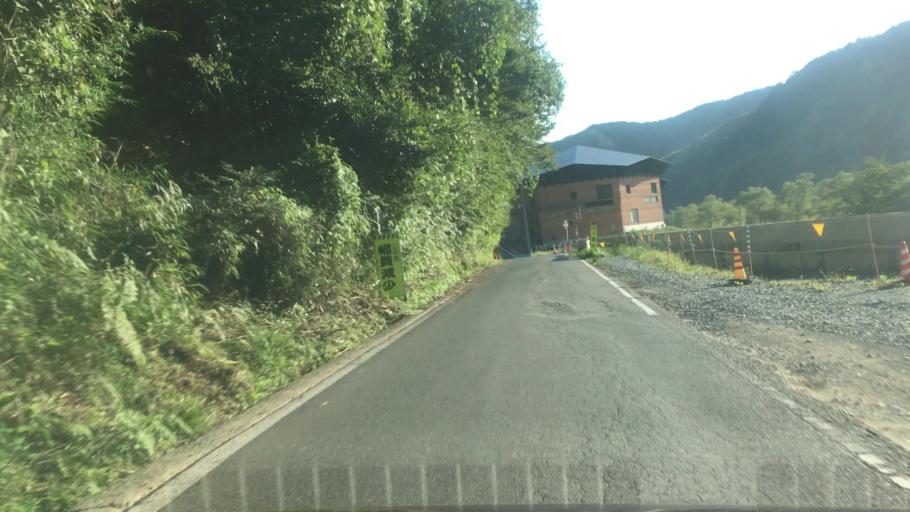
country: JP
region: Hyogo
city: Toyooka
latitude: 35.5904
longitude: 134.8041
